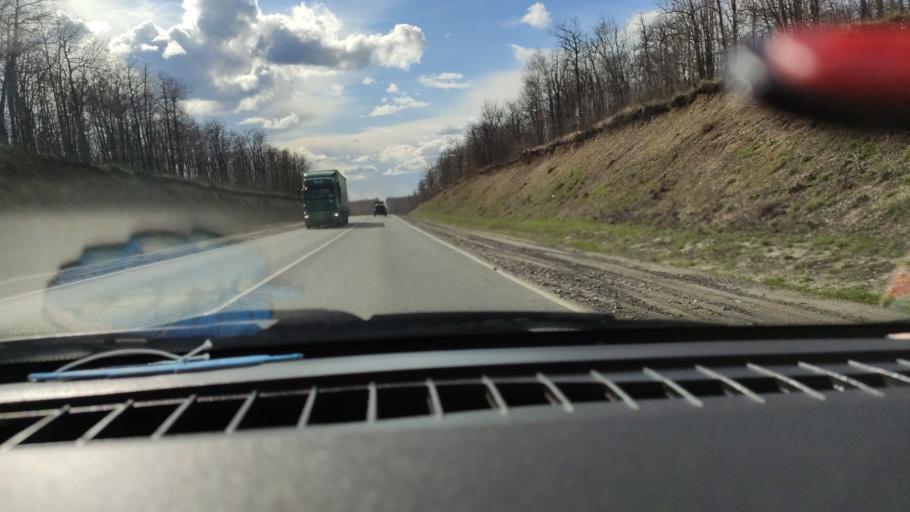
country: RU
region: Saratov
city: Vol'sk
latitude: 52.1083
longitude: 47.3919
